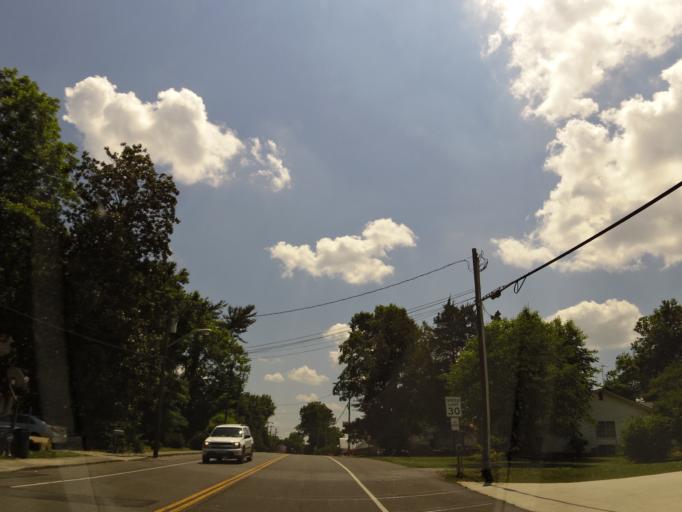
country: US
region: Tennessee
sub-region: Rhea County
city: Dayton
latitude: 35.4995
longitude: -85.0089
